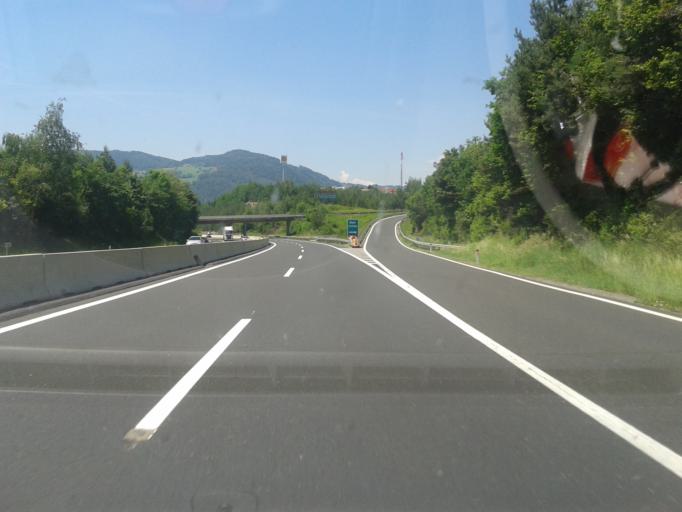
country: AT
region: Carinthia
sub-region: Politischer Bezirk Volkermarkt
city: Voelkermarkt
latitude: 46.6787
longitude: 14.6025
